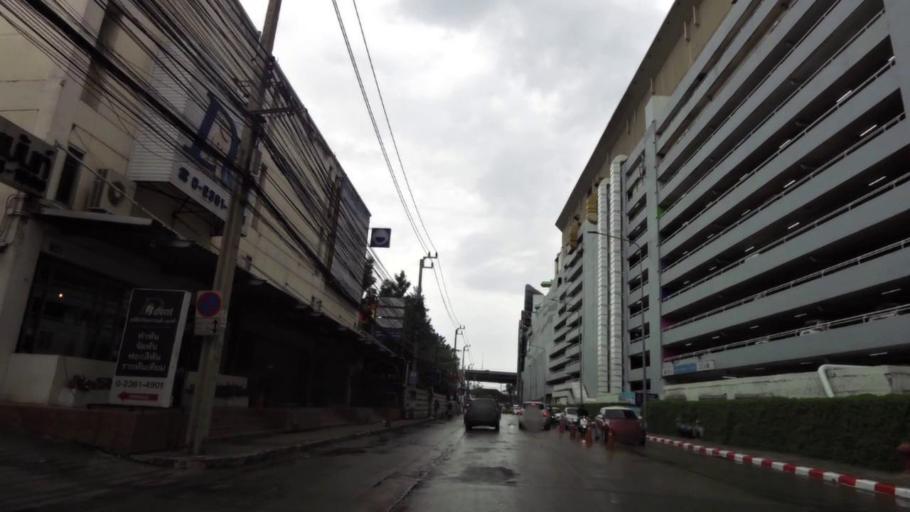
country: TH
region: Bangkok
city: Bang Na
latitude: 13.6704
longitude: 100.6356
